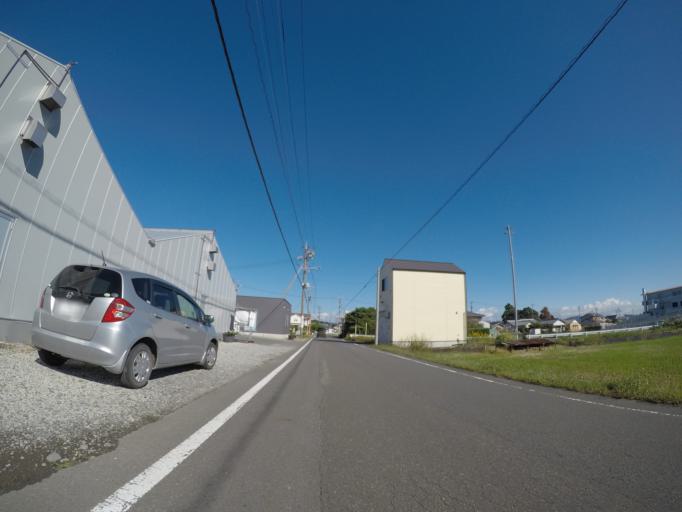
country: JP
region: Shizuoka
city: Fujieda
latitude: 34.8354
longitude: 138.2392
